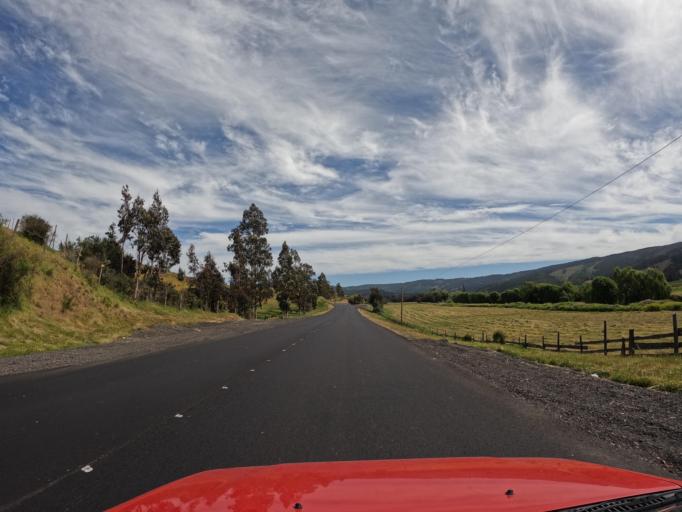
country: CL
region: Maule
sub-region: Provincia de Talca
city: Constitucion
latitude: -35.0699
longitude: -72.0383
